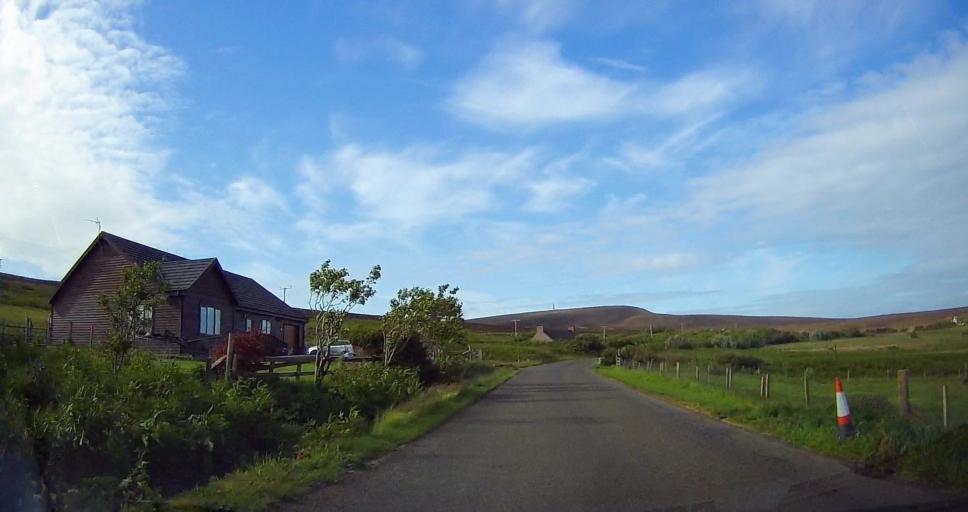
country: GB
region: Scotland
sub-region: Orkney Islands
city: Stromness
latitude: 58.7973
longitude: -3.2519
